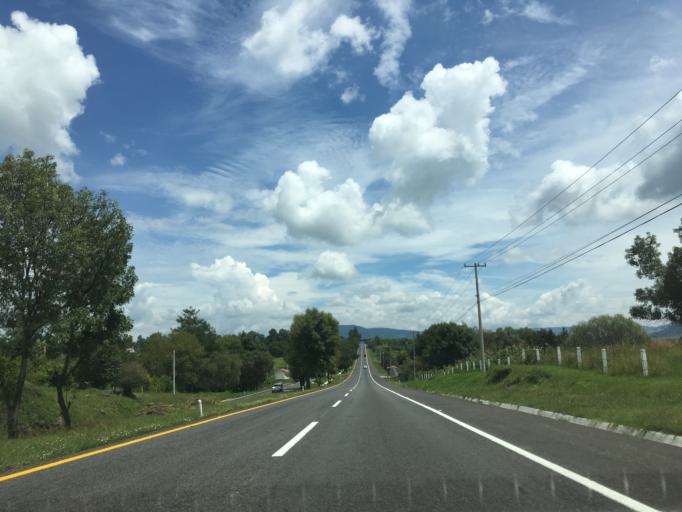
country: MX
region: Michoacan
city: Lagunillas
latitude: 19.5576
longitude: -101.3963
